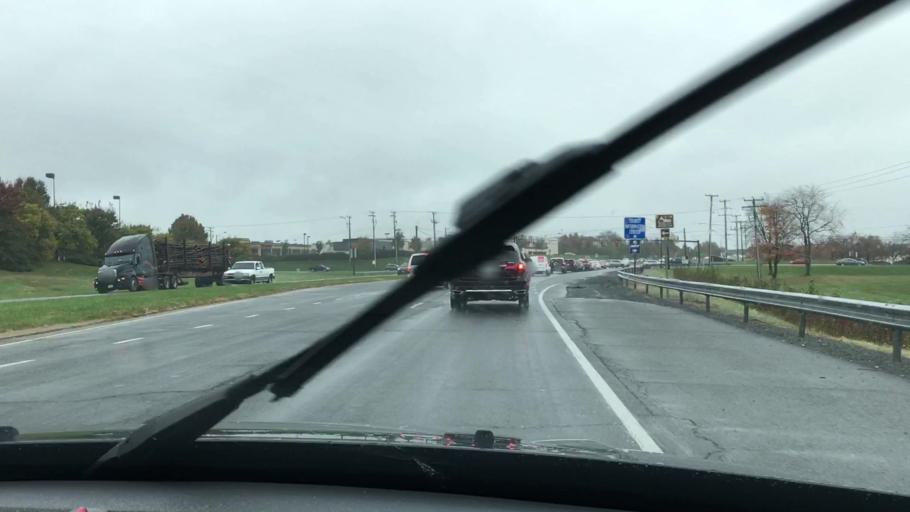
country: US
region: Virginia
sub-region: Loudoun County
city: Leesburg
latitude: 39.1153
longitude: -77.5384
